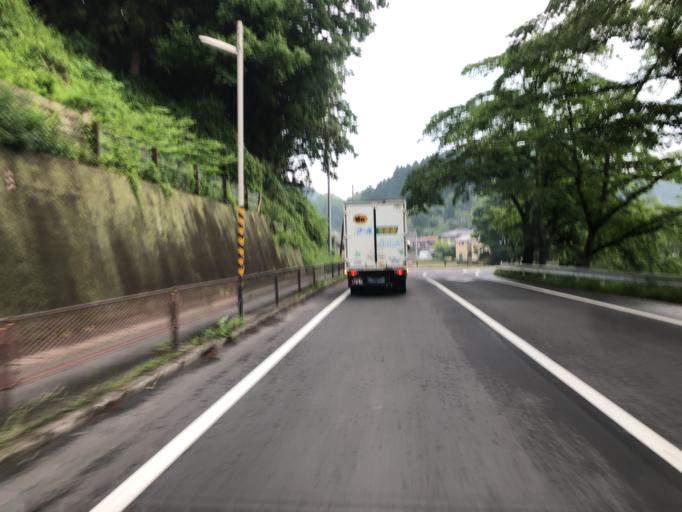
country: JP
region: Fukushima
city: Ishikawa
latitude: 37.1459
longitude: 140.4527
